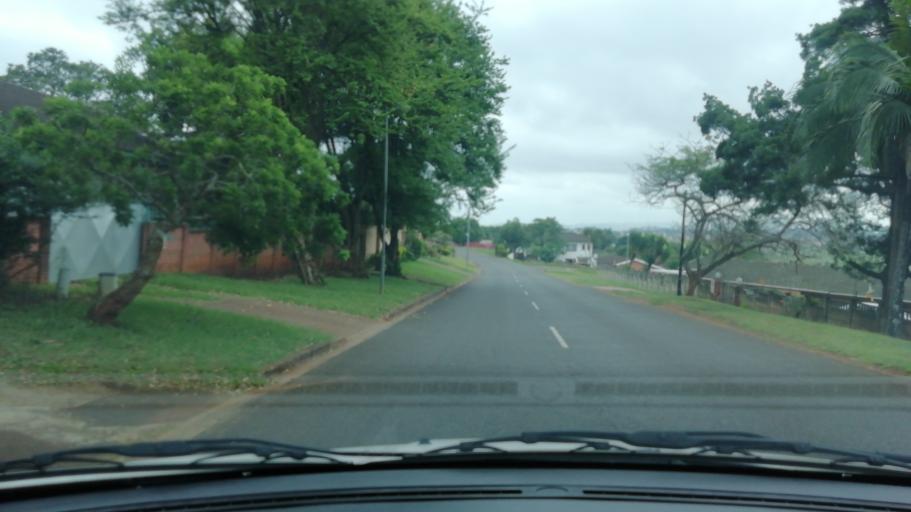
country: ZA
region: KwaZulu-Natal
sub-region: uThungulu District Municipality
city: Empangeni
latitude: -28.7643
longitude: 31.8903
